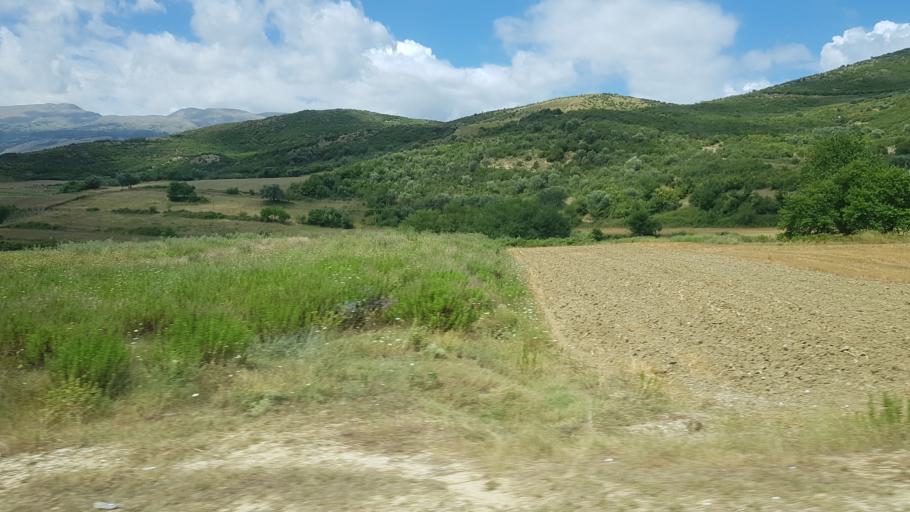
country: AL
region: Gjirokaster
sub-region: Rrethi i Tepelenes
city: Krahes
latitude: 40.4091
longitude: 19.8599
